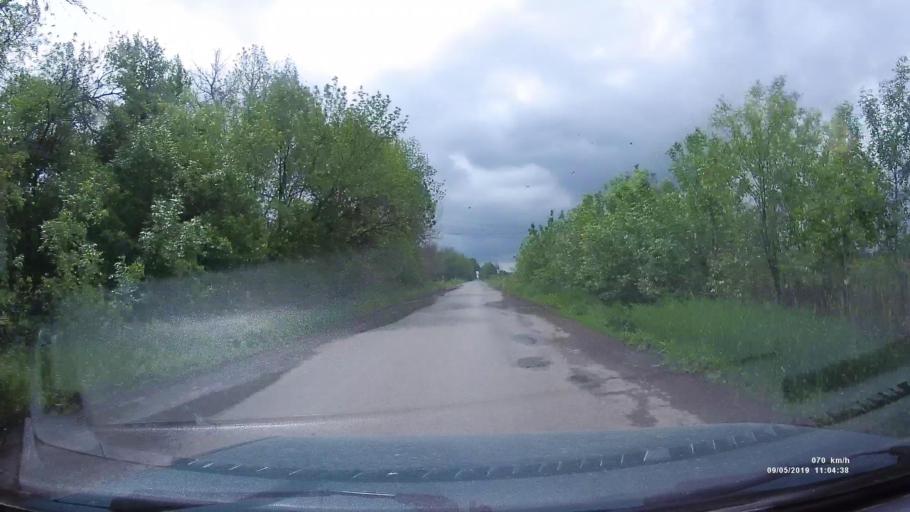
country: RU
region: Krasnodarskiy
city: Kanelovskaya
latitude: 46.8148
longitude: 39.2099
